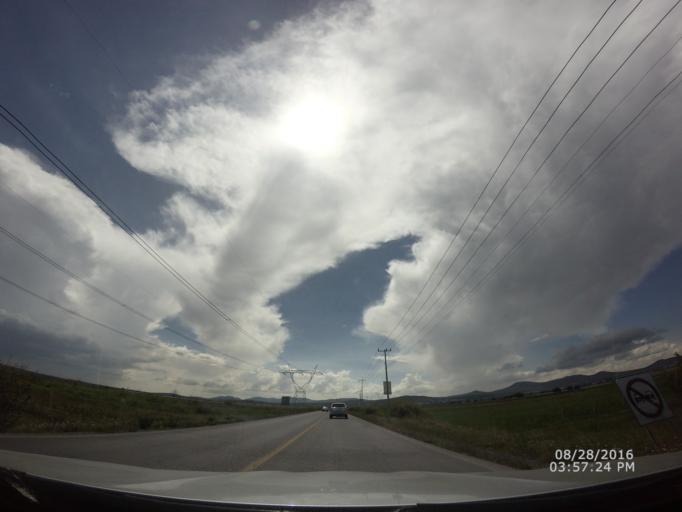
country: MX
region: Hidalgo
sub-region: Mineral de la Reforma
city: La Colonia
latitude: 20.0353
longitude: -98.7667
